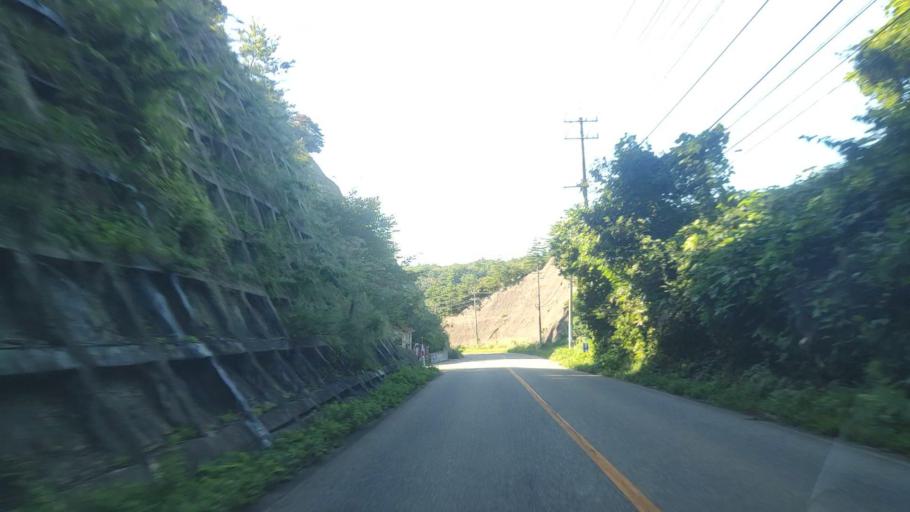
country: JP
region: Ishikawa
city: Nanao
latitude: 37.3156
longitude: 137.1619
